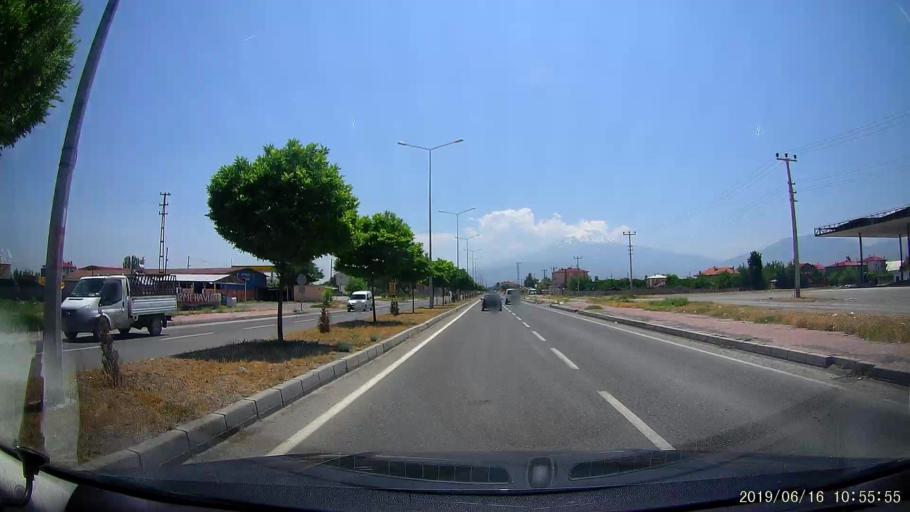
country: TR
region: Igdir
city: Igdir
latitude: 39.9335
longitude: 44.0156
